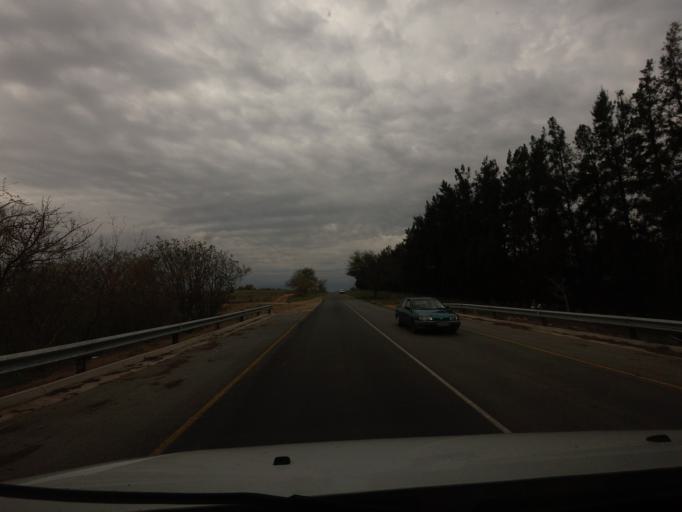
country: ZA
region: Limpopo
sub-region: Mopani District Municipality
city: Hoedspruit
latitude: -24.4489
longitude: 30.8601
